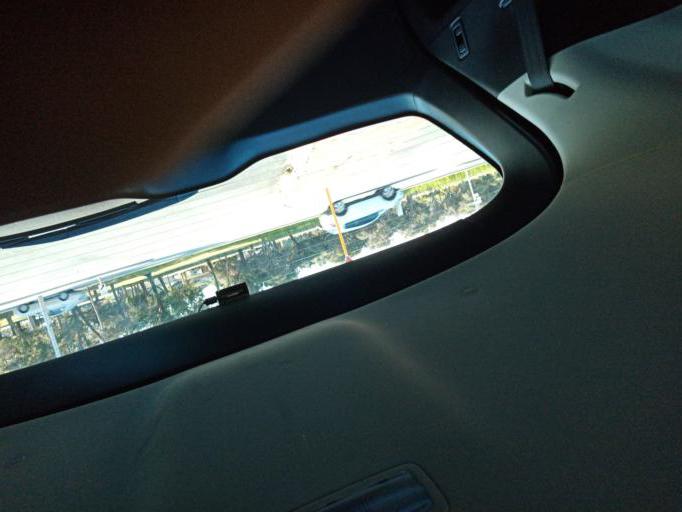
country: AU
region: Western Australia
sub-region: City of Cockburn
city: South Lake
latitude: -32.1179
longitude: 115.8406
